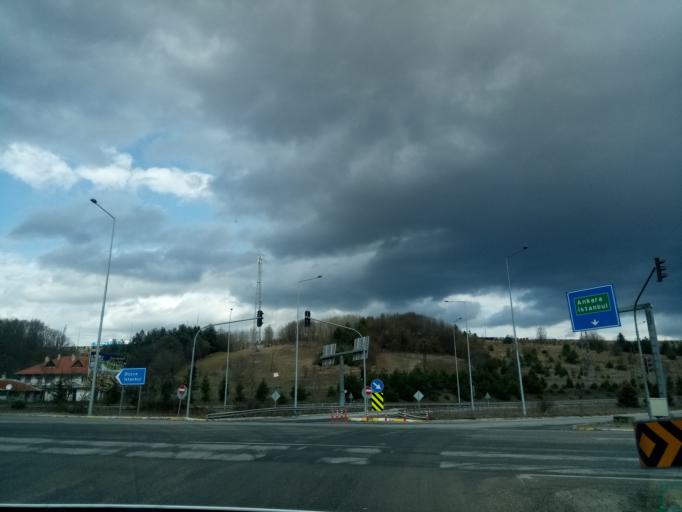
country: TR
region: Bolu
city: Bolu
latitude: 40.7123
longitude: 31.4817
